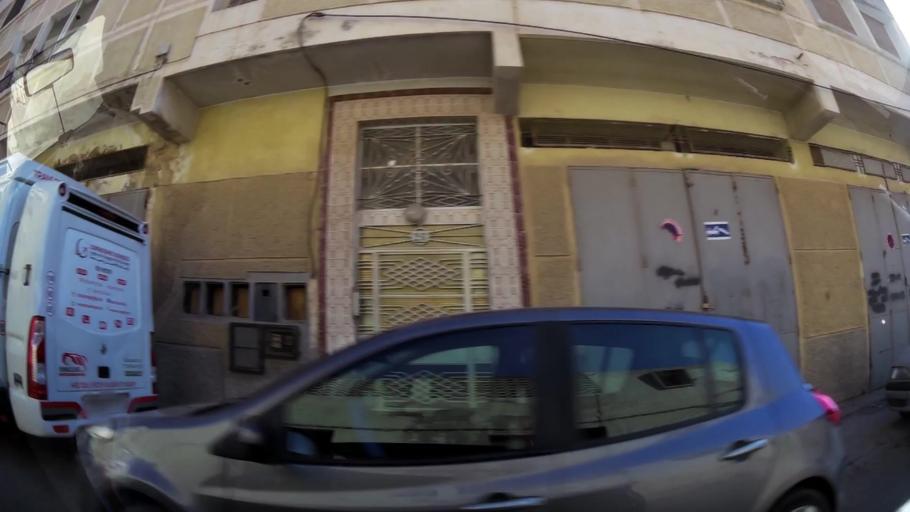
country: MA
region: Oriental
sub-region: Oujda-Angad
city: Oujda
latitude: 34.6892
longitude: -1.9151
